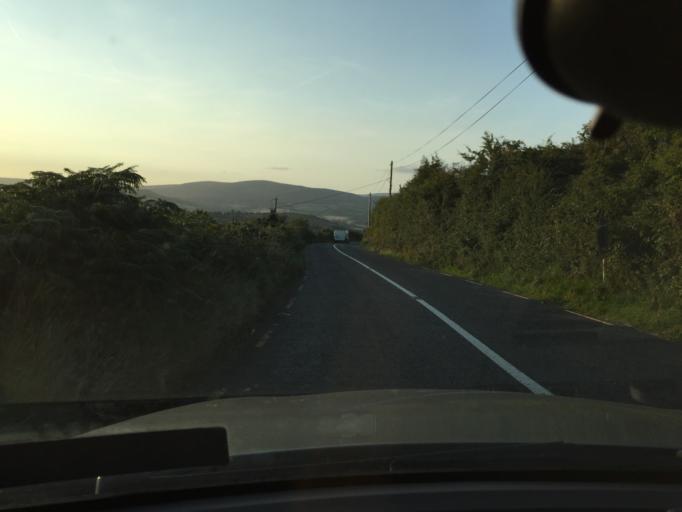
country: IE
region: Leinster
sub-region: Wicklow
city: Kilmacanoge
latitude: 53.1512
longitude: -6.1646
